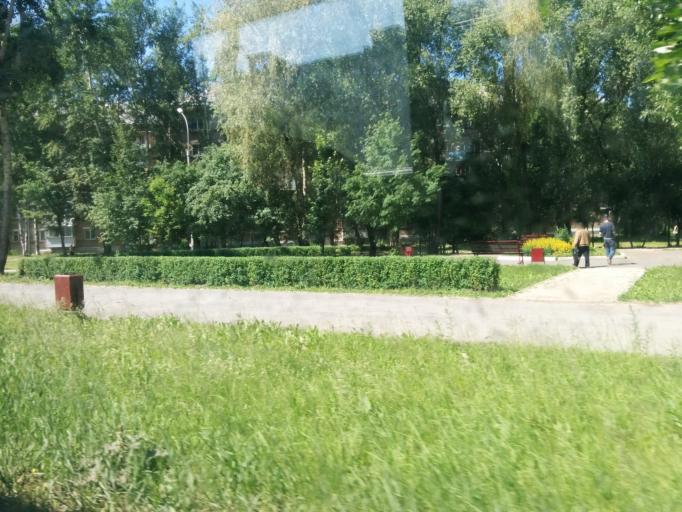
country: RU
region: Perm
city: Perm
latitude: 57.9997
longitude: 56.2960
